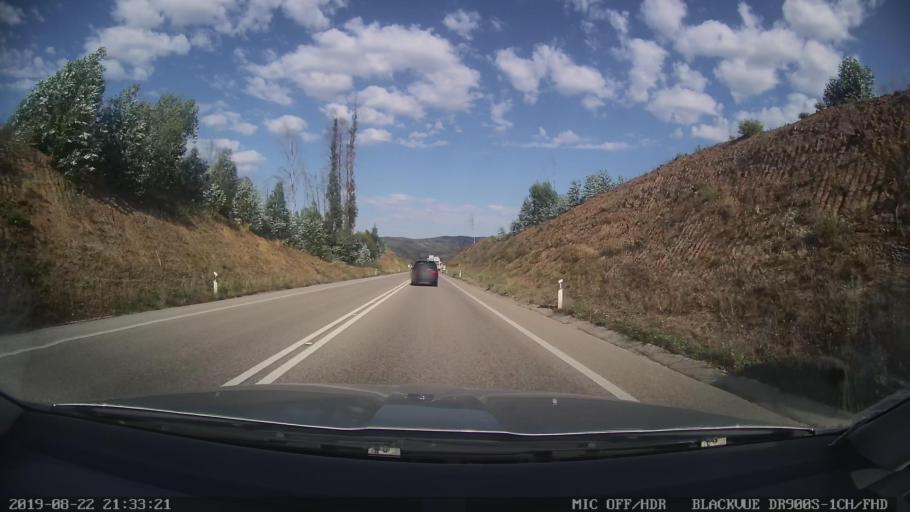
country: PT
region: Leiria
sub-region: Pedrogao Grande
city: Pedrogao Grande
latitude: 39.9265
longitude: -8.1763
